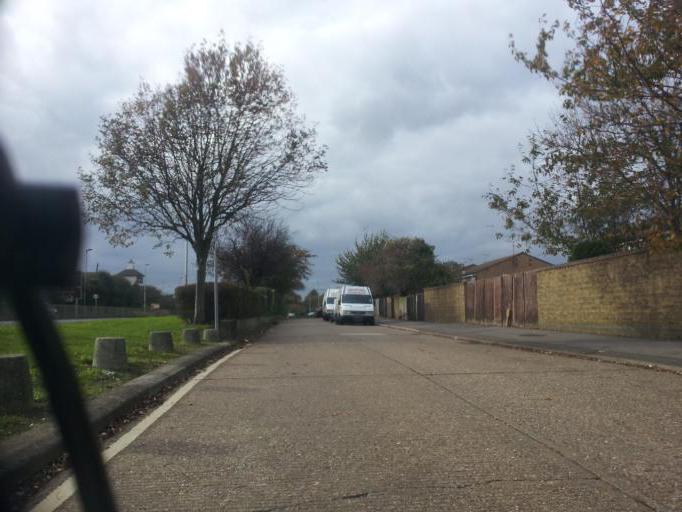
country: GB
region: England
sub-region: Kent
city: Gillingham
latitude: 51.3705
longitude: 0.5720
